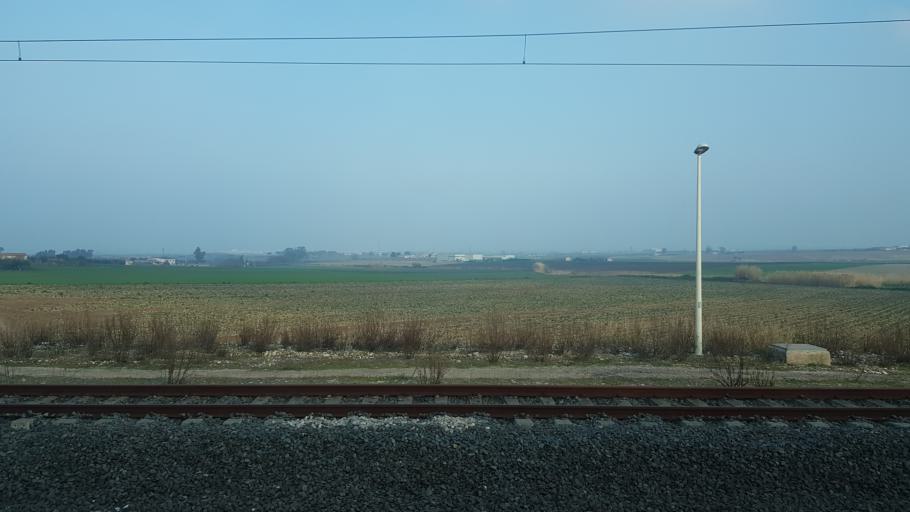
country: IT
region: Apulia
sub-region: Provincia di Foggia
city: Lesina
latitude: 41.8529
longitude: 15.2958
